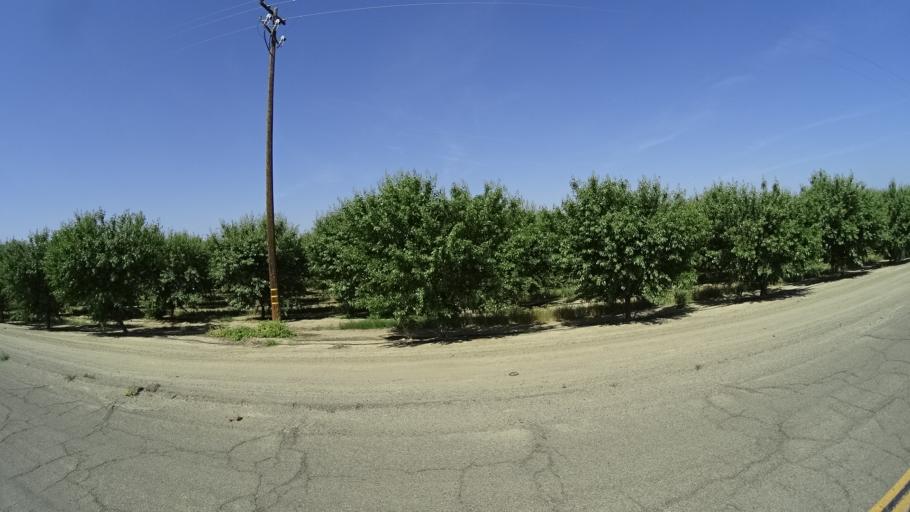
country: US
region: California
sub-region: Kings County
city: Kettleman City
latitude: 36.0517
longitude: -120.0036
